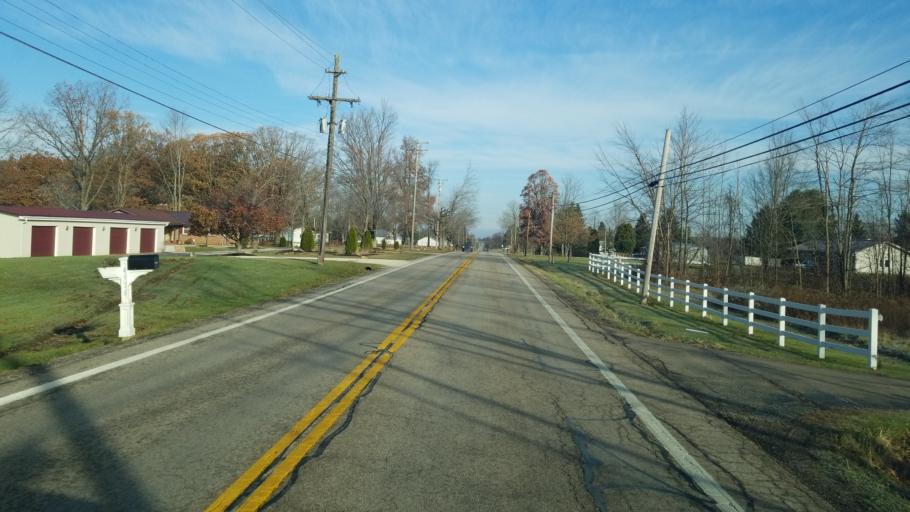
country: US
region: Ohio
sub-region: Ashtabula County
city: North Kingsville
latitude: 41.8608
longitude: -80.6662
